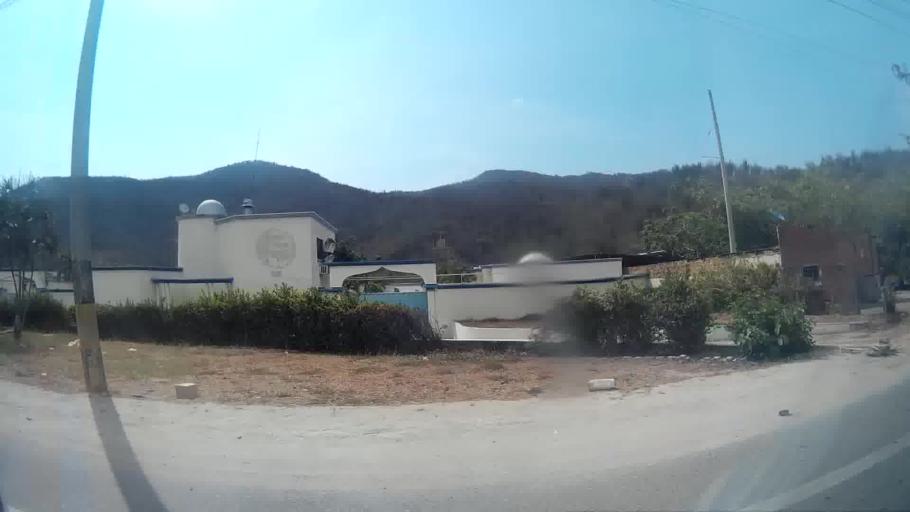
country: CO
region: Magdalena
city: Santa Marta
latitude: 11.1933
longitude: -74.2065
